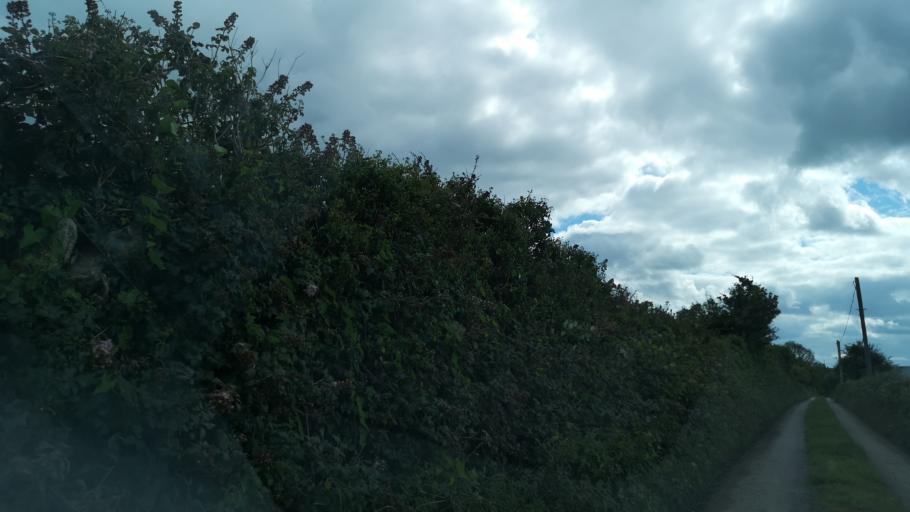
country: IE
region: Connaught
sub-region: County Galway
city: Moycullen
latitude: 53.3192
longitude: -9.1335
